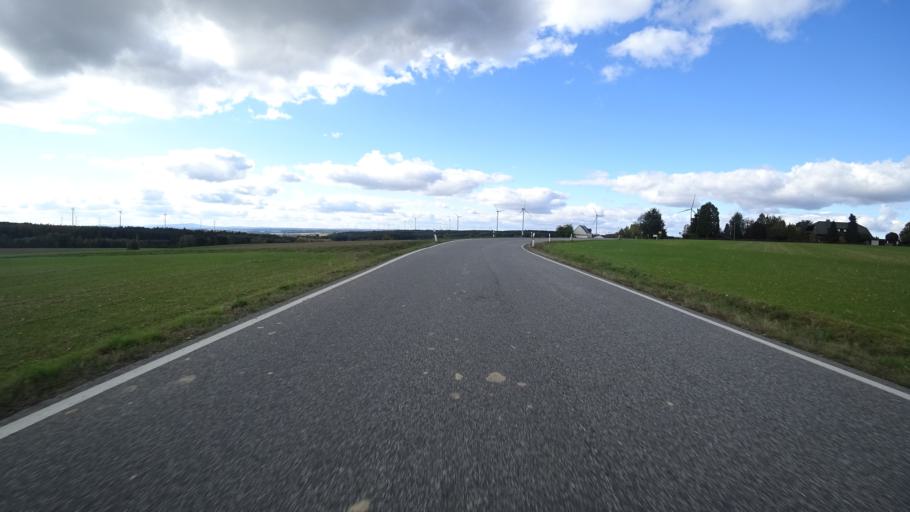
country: DE
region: Rheinland-Pfalz
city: Liebshausen
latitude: 50.0303
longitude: 7.6346
